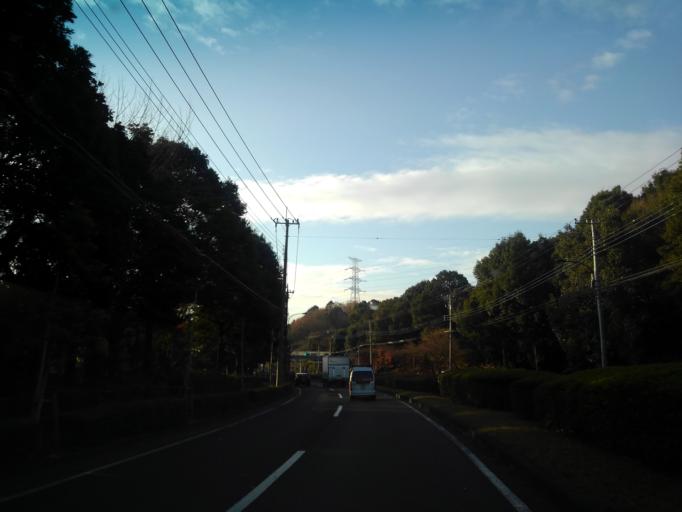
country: JP
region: Tokyo
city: Hino
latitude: 35.6186
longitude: 139.4426
